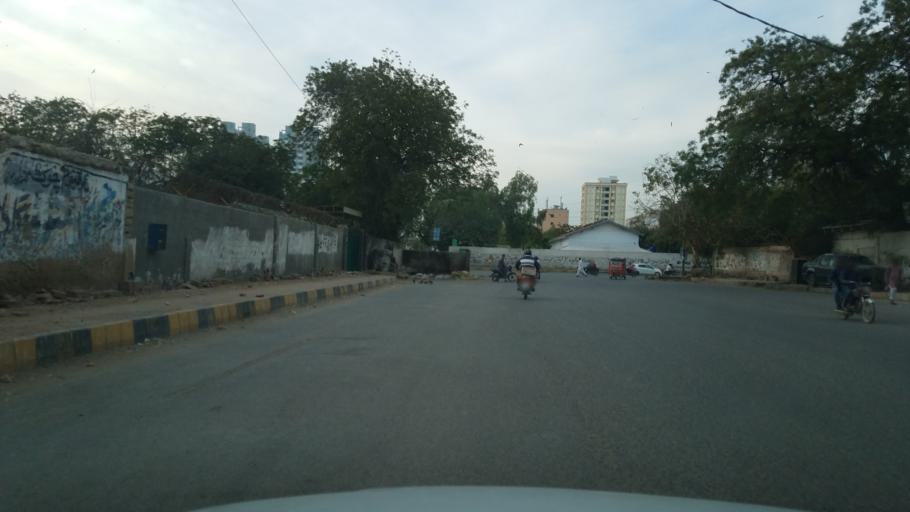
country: PK
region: Sindh
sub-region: Karachi District
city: Karachi
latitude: 24.8680
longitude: 67.0275
